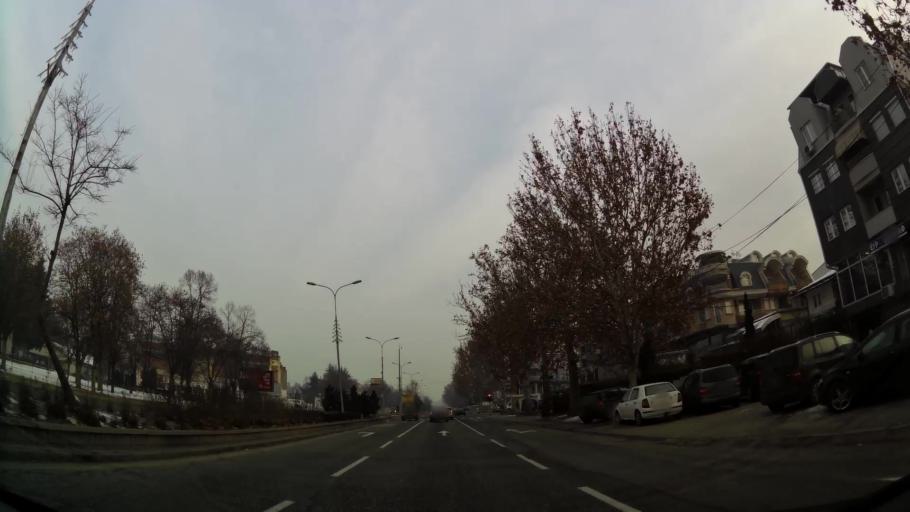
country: MK
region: Cair
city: Cair
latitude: 42.0207
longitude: 21.4489
